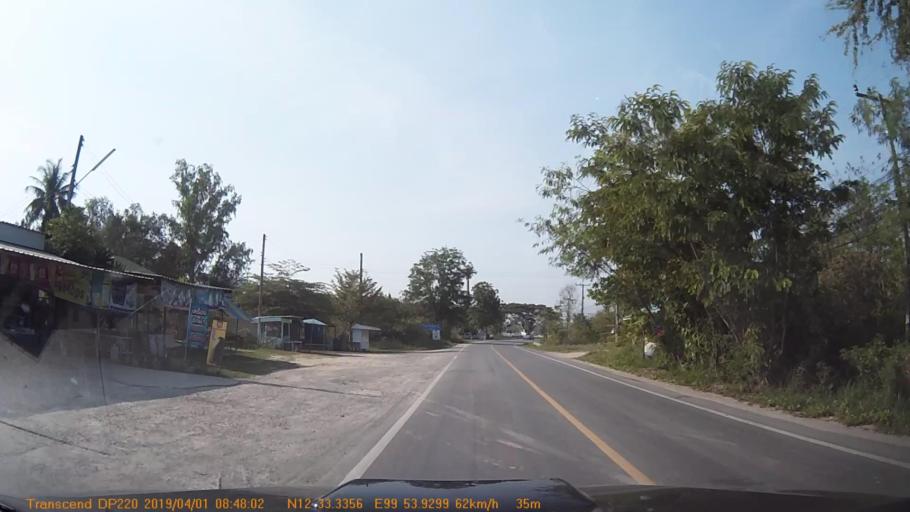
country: TH
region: Prachuap Khiri Khan
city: Hua Hin
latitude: 12.5553
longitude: 99.8988
